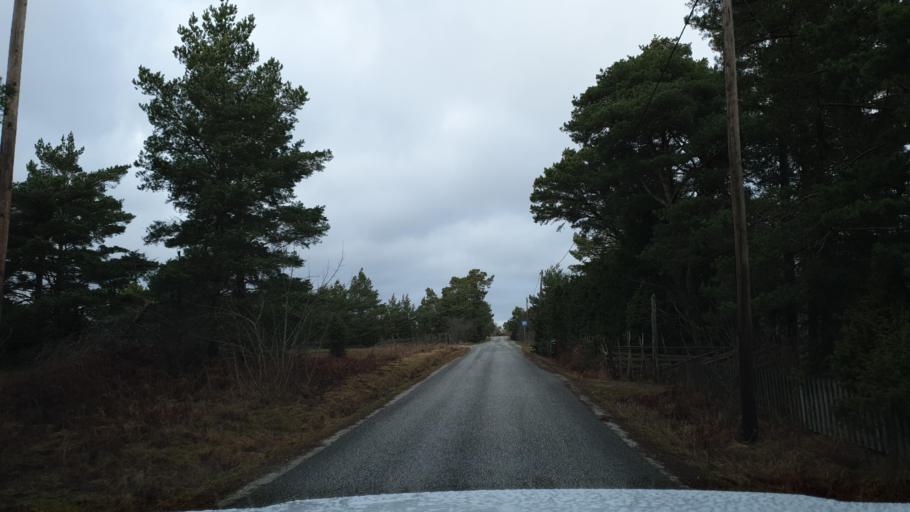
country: SE
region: Gotland
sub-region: Gotland
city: Slite
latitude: 57.3863
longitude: 18.8085
